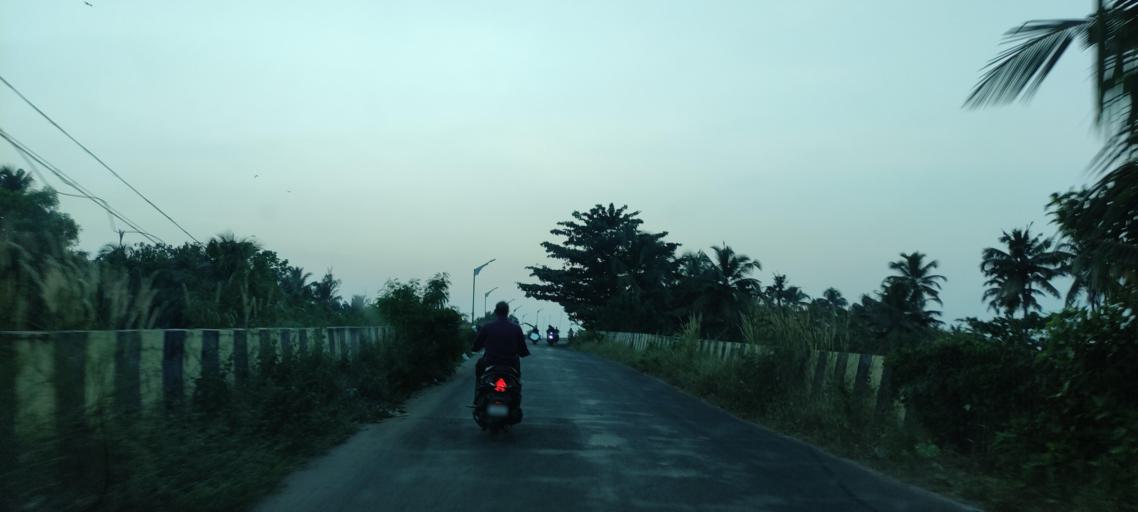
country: IN
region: Kerala
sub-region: Alappuzha
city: Kayankulam
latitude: 9.1165
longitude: 76.4800
